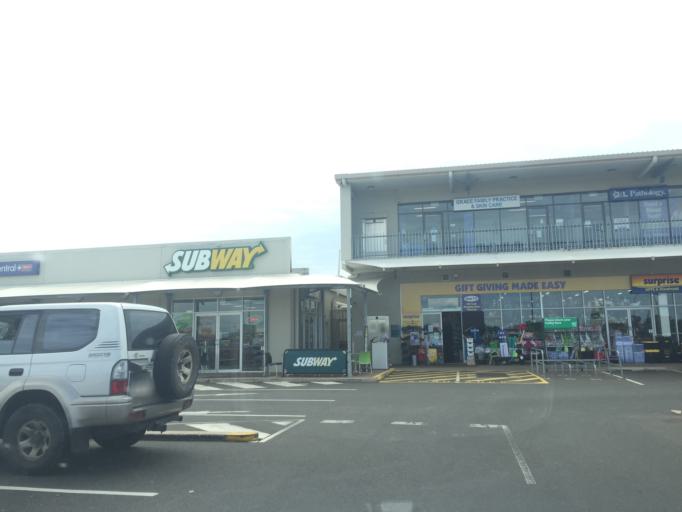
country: AU
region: Queensland
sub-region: Bundaberg
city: Bundaberg
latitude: -24.8185
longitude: 152.4560
